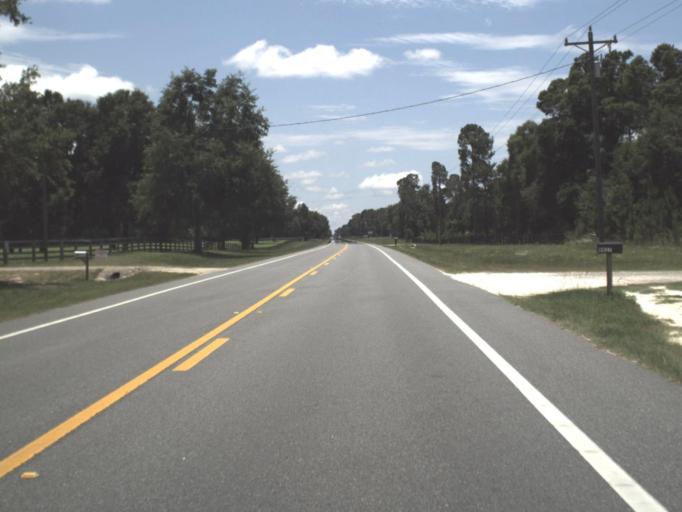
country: US
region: Florida
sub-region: Dixie County
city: Cross City
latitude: 29.7455
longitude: -82.9847
